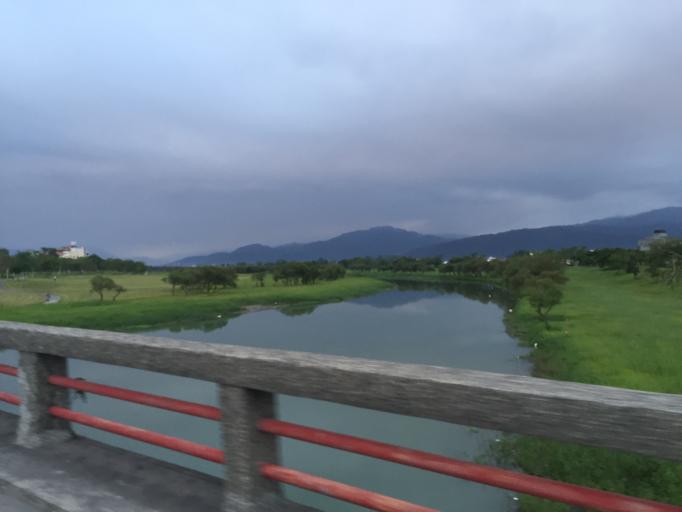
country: TW
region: Taiwan
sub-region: Yilan
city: Yilan
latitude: 24.7664
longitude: 121.7554
